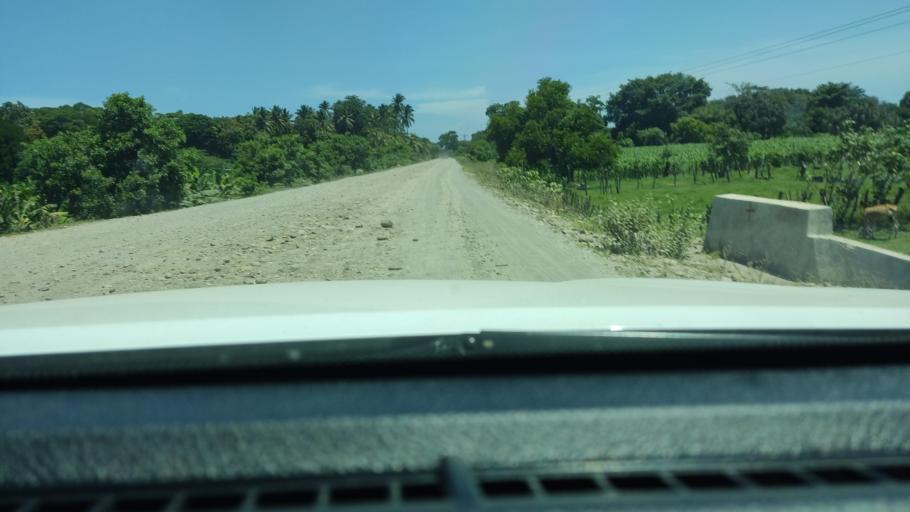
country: SV
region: Ahuachapan
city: San Francisco Menendez
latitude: 13.7928
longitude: -90.1172
